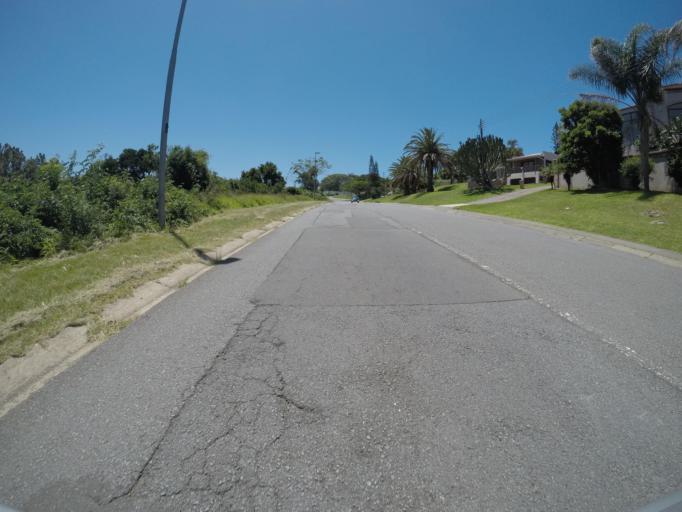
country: ZA
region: Eastern Cape
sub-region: Buffalo City Metropolitan Municipality
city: East London
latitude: -32.9791
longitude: 27.9395
